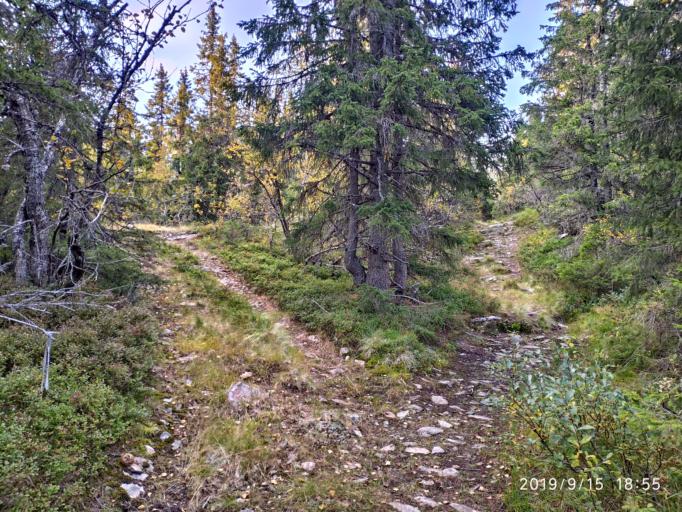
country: NO
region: Oppland
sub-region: Oyer
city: Tretten
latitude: 61.4130
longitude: 10.2638
